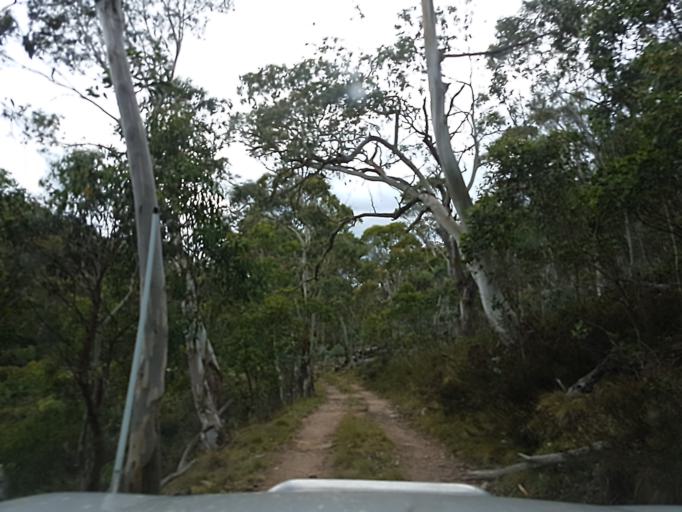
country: AU
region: New South Wales
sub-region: Snowy River
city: Jindabyne
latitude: -36.8897
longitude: 148.1232
